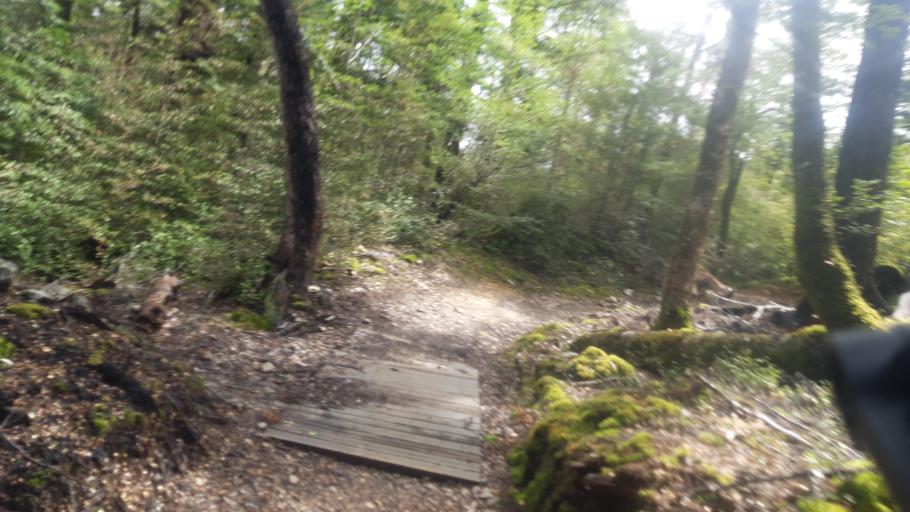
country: NZ
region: Tasman
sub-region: Tasman District
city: Wakefield
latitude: -41.7809
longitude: 172.8212
